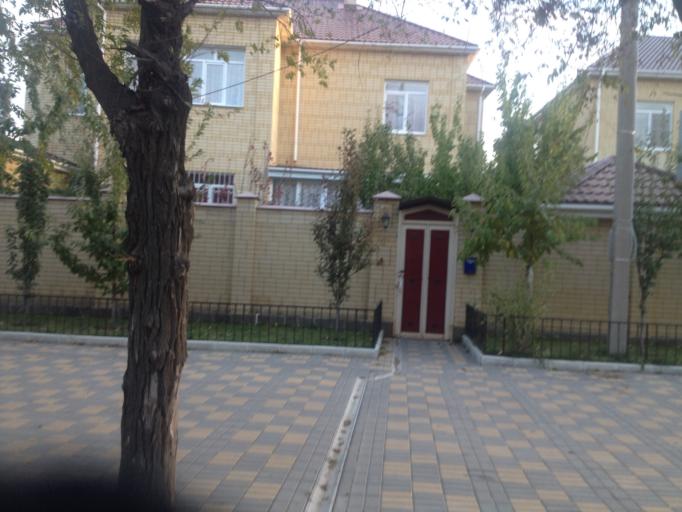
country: RU
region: Volgograd
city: Volgograd
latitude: 48.7385
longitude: 44.5079
